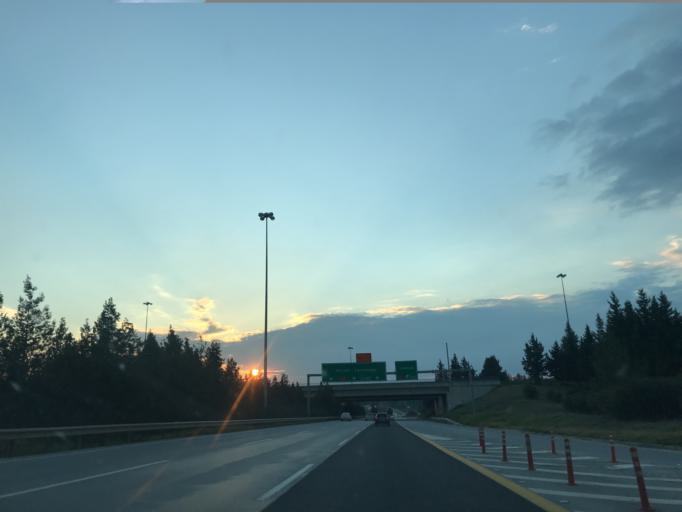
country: TR
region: Mersin
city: Yenice
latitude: 37.0080
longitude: 34.9665
